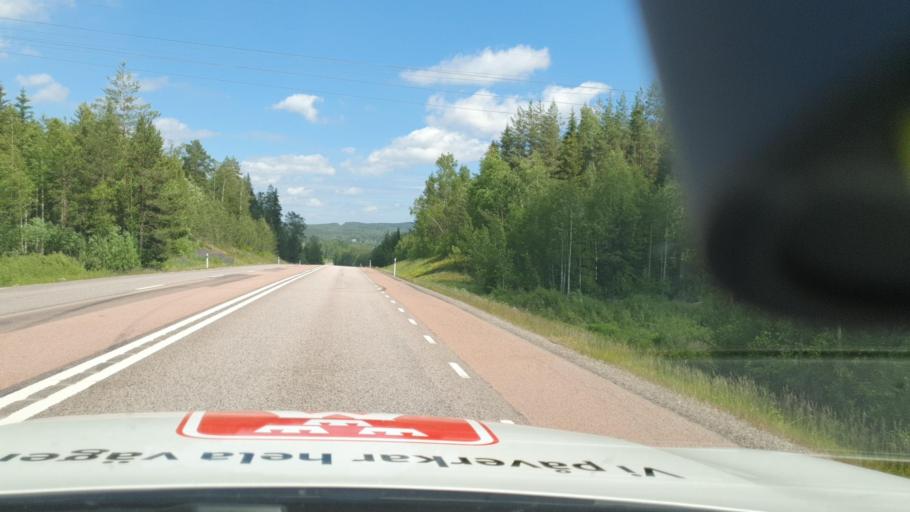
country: SE
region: Vaermland
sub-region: Filipstads Kommun
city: Filipstad
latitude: 59.7062
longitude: 14.1286
